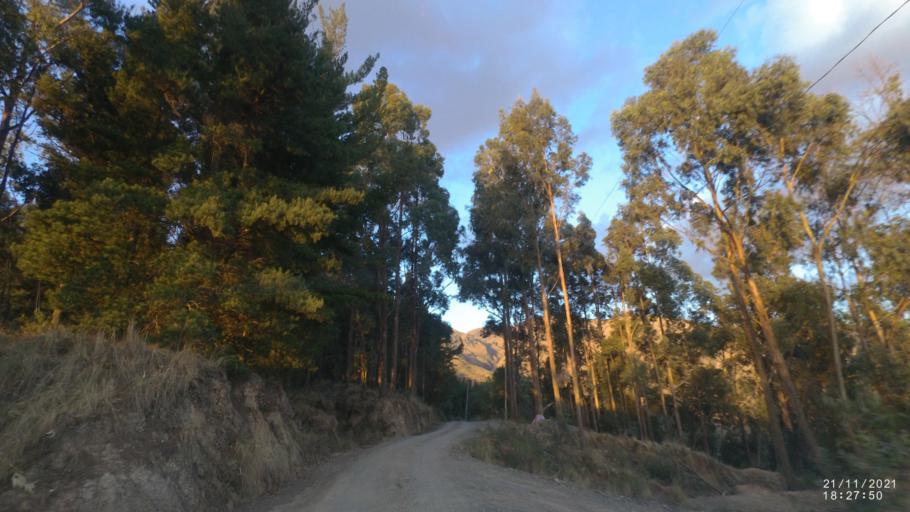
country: BO
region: Cochabamba
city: Cochabamba
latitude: -17.3072
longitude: -66.2183
